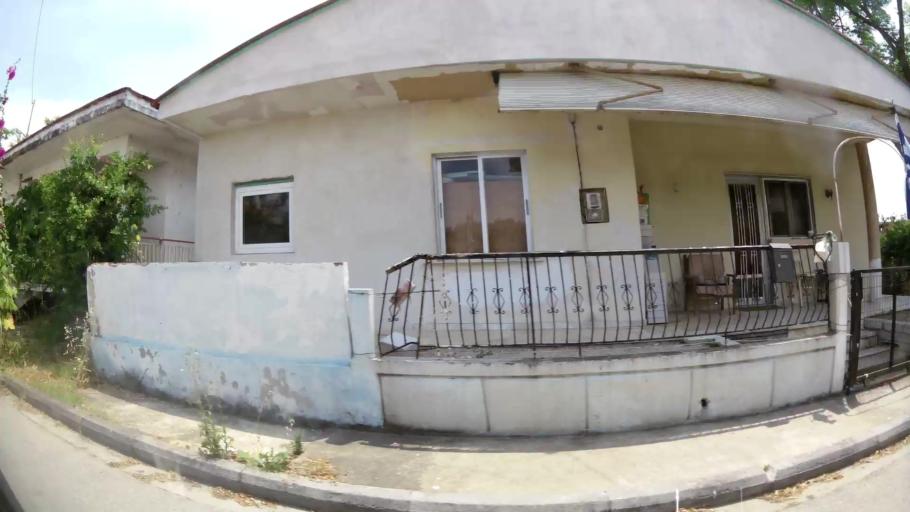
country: GR
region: Central Macedonia
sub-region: Nomos Pierias
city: Peristasi
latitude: 40.2634
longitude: 22.5364
